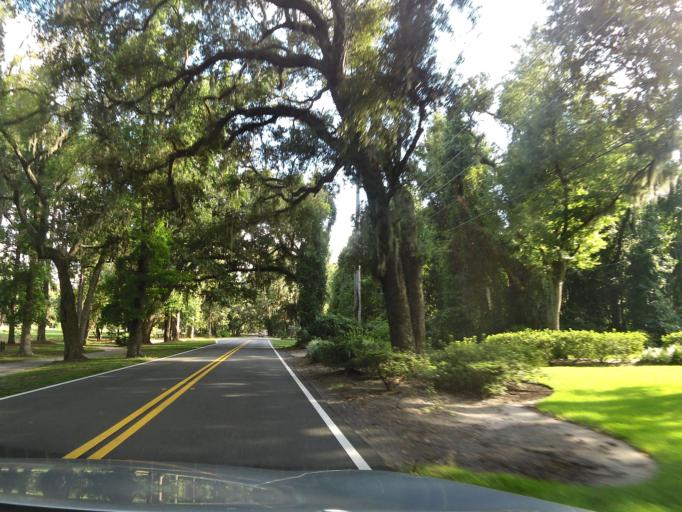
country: US
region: Georgia
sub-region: Glynn County
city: Saint Simon Mills
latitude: 31.1994
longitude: -81.3761
